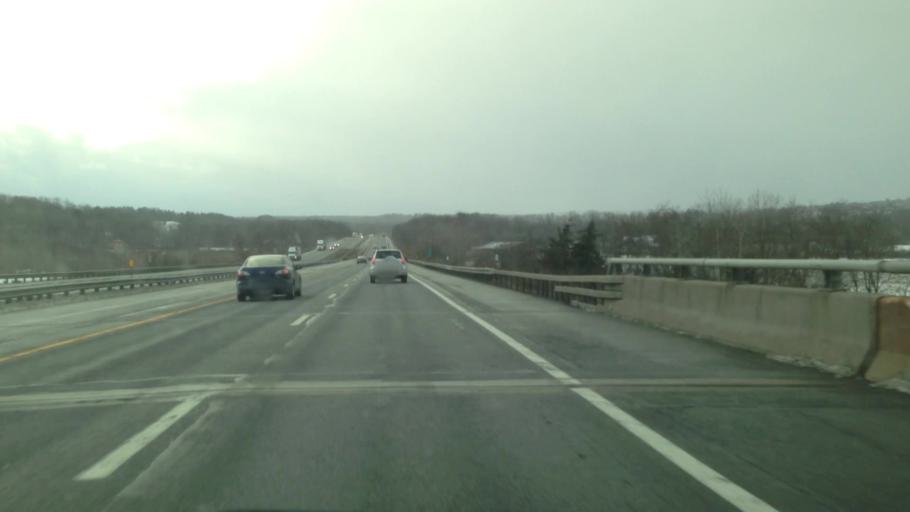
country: US
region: New York
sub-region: Montgomery County
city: Tribes Hill
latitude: 42.9316
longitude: -74.2799
